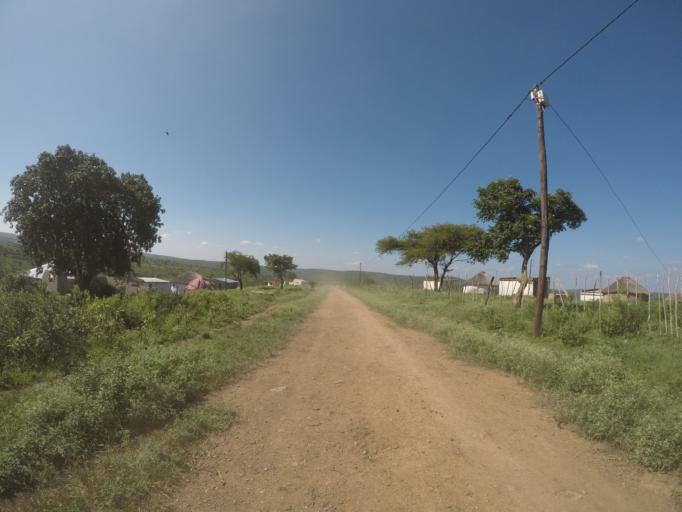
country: ZA
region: KwaZulu-Natal
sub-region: uThungulu District Municipality
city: Empangeni
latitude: -28.5577
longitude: 31.7052
